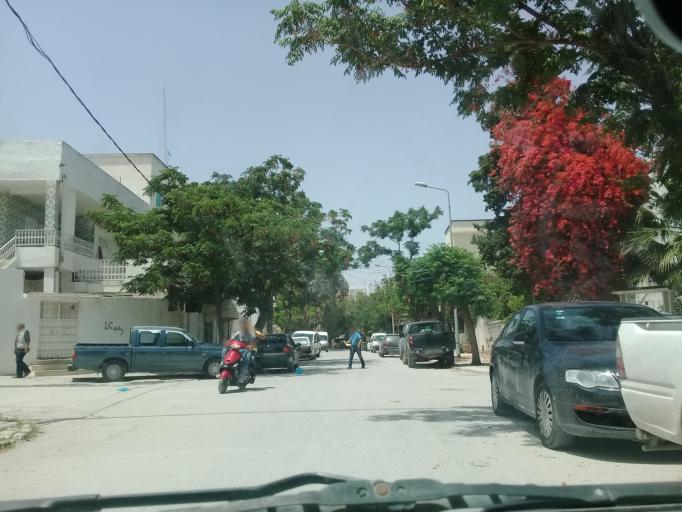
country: TN
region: Ariana
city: Ariana
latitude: 36.8300
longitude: 10.1950
